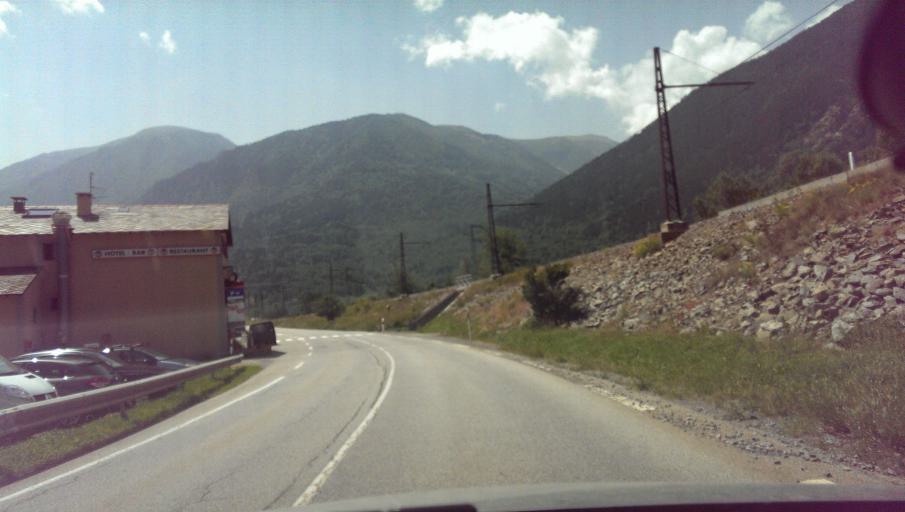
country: ES
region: Catalonia
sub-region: Provincia de Girona
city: Meranges
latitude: 42.5269
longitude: 1.8236
